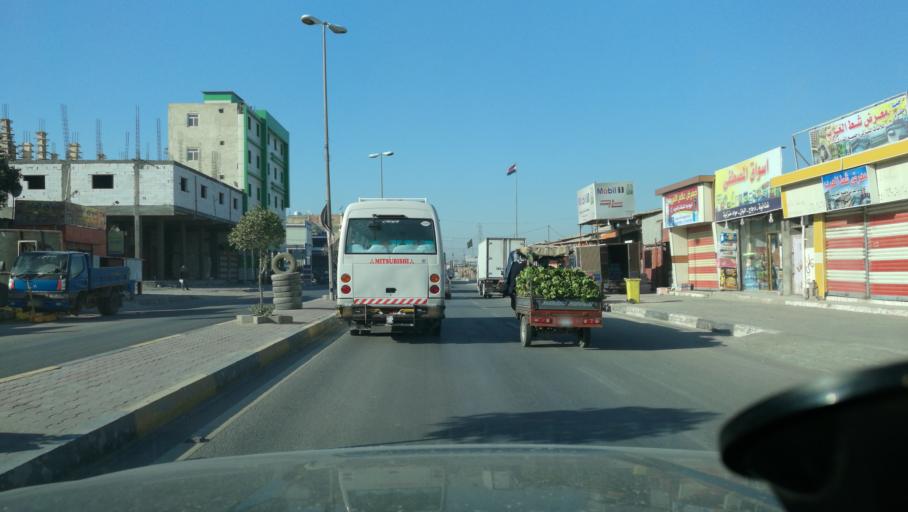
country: IQ
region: Basra Governorate
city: Al Basrah al Qadimah
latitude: 30.4855
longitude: 47.8065
